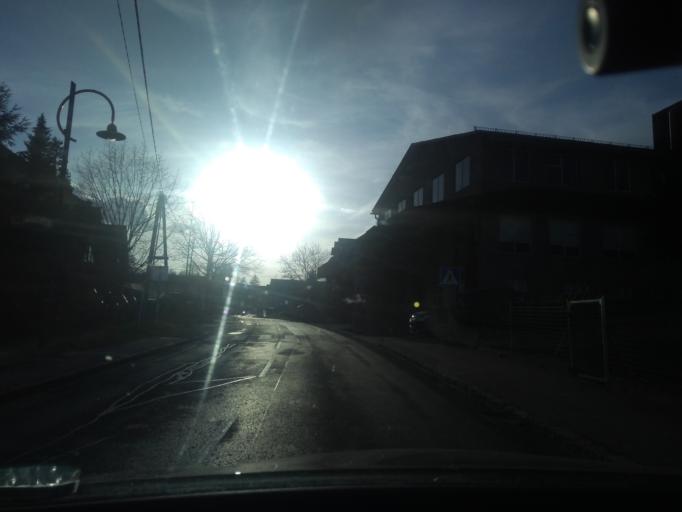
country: AT
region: Styria
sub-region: Politischer Bezirk Suedoststeiermark
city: Jagerberg
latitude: 46.8542
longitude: 15.7423
